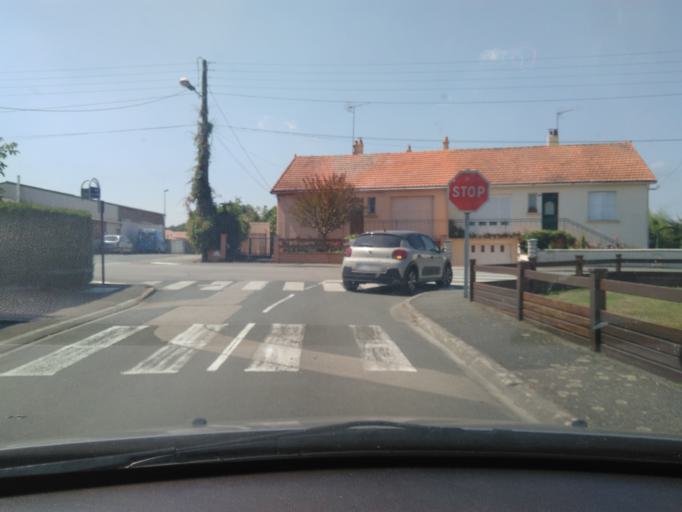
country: FR
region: Pays de la Loire
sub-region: Departement de la Vendee
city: La Ferriere
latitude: 46.7101
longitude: -1.3121
